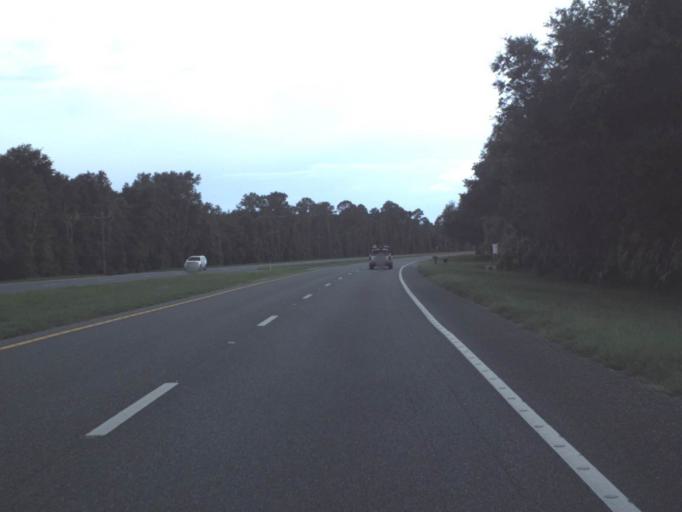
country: US
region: Florida
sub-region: Levy County
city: Inglis
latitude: 29.0943
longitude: -82.6361
